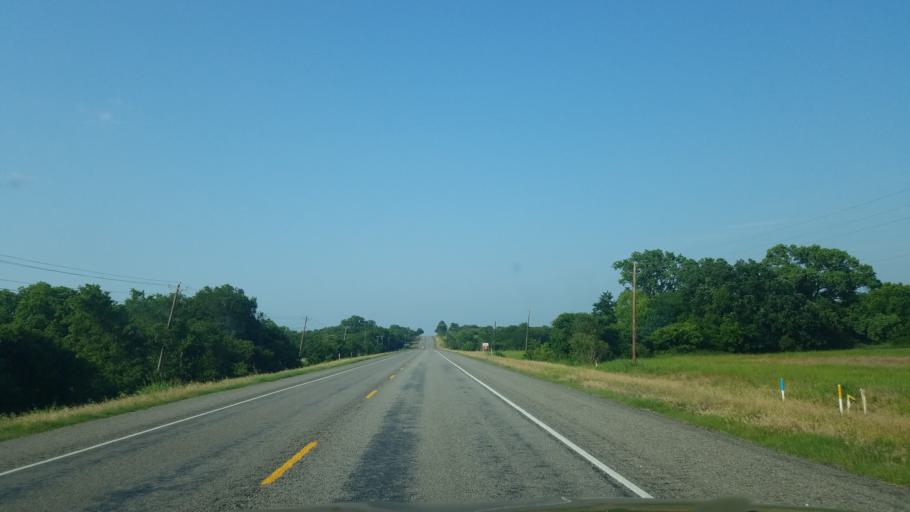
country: US
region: Texas
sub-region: Denton County
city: Denton
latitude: 33.2860
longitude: -97.0876
